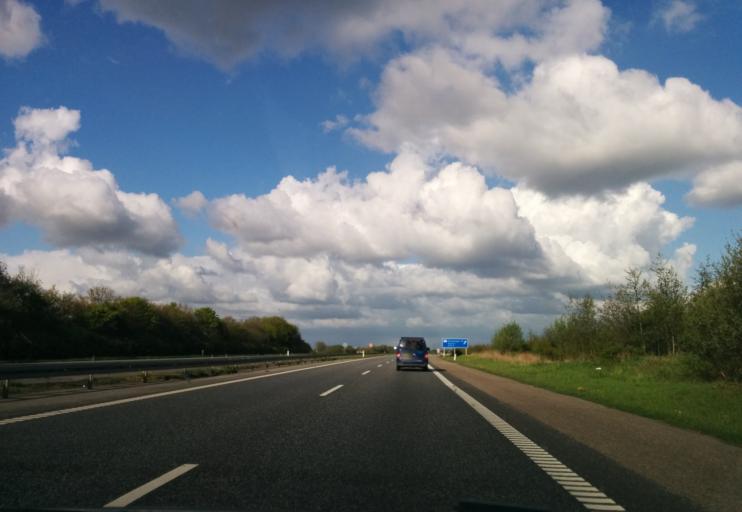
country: DK
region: Central Jutland
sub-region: Arhus Kommune
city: Kolt
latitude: 56.1178
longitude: 10.0734
